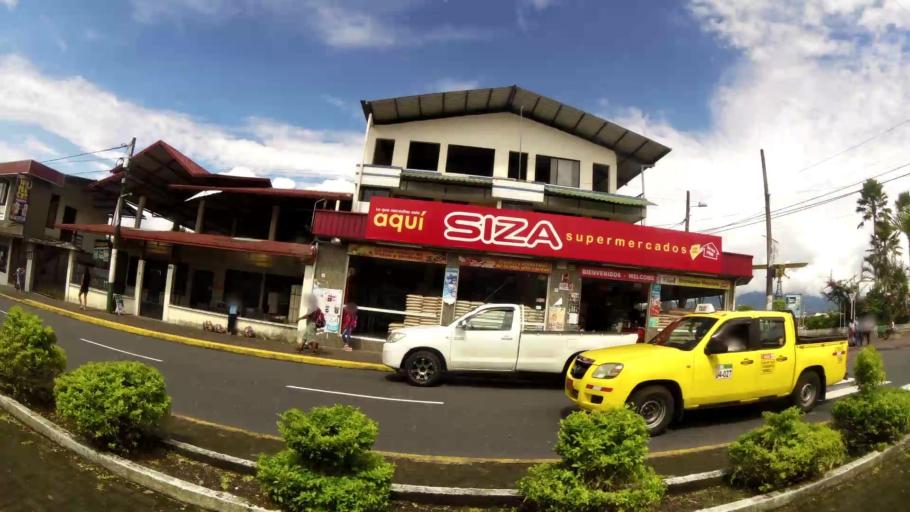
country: EC
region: Pastaza
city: Puyo
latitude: -1.5004
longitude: -78.0612
